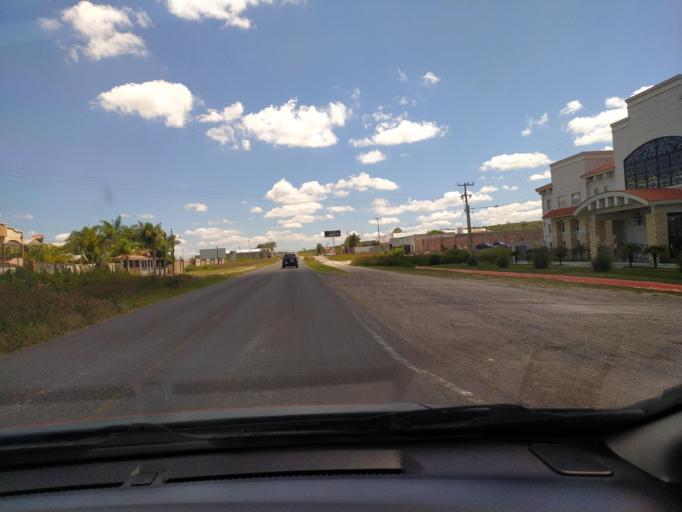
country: MX
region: Jalisco
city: San Julian
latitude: 21.0073
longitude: -102.1458
